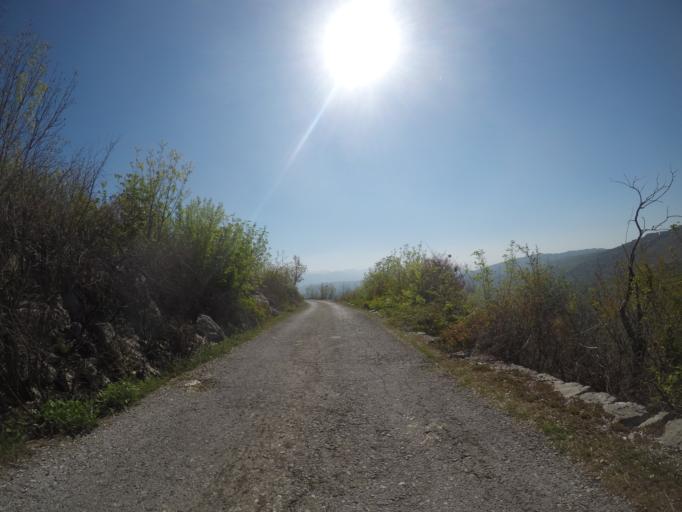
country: ME
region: Danilovgrad
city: Danilovgrad
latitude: 42.5148
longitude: 19.0718
